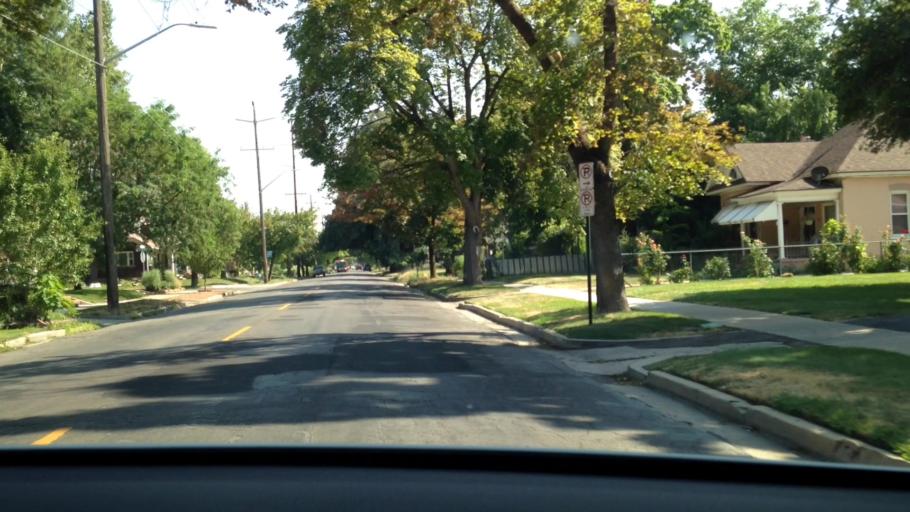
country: US
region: Utah
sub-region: Salt Lake County
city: South Salt Lake
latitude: 40.7325
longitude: -111.8768
